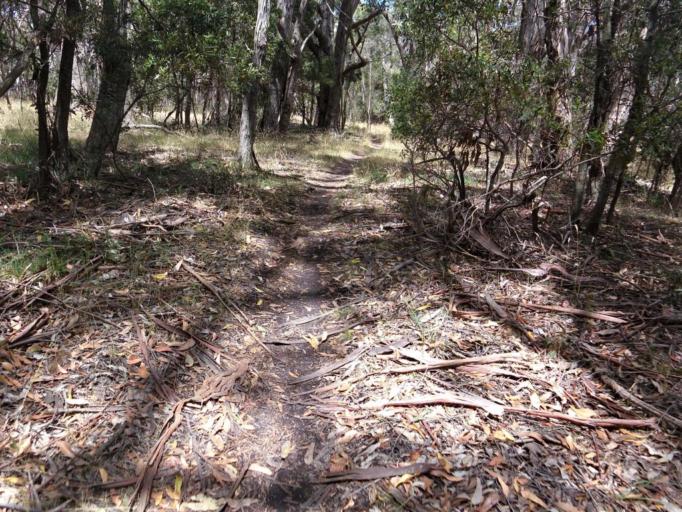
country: AU
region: Victoria
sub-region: Melton
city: Melton West
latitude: -37.4796
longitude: 144.5378
